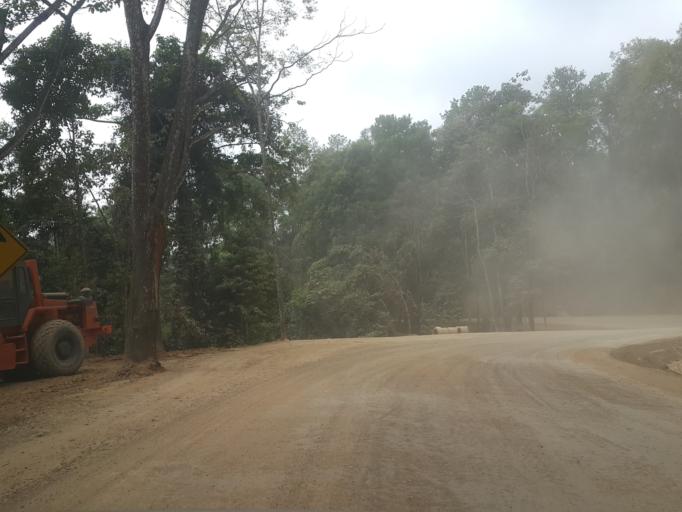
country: TH
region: Mae Hong Son
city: Mae Hi
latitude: 19.2360
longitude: 98.6618
